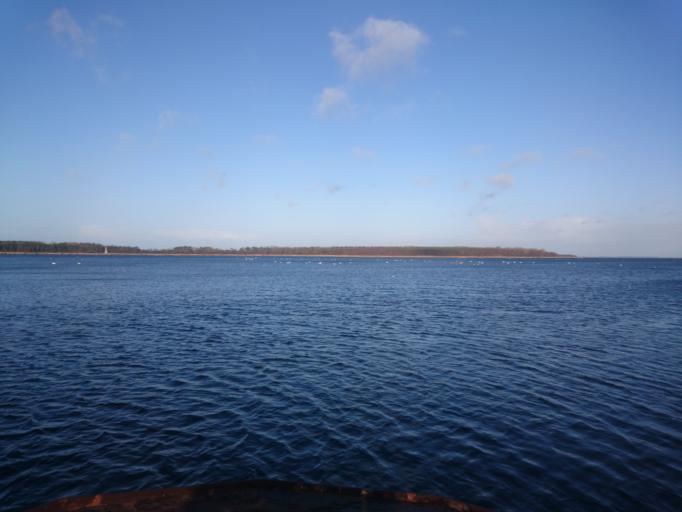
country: DE
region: Mecklenburg-Vorpommern
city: Prohn
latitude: 54.4343
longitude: 13.0329
